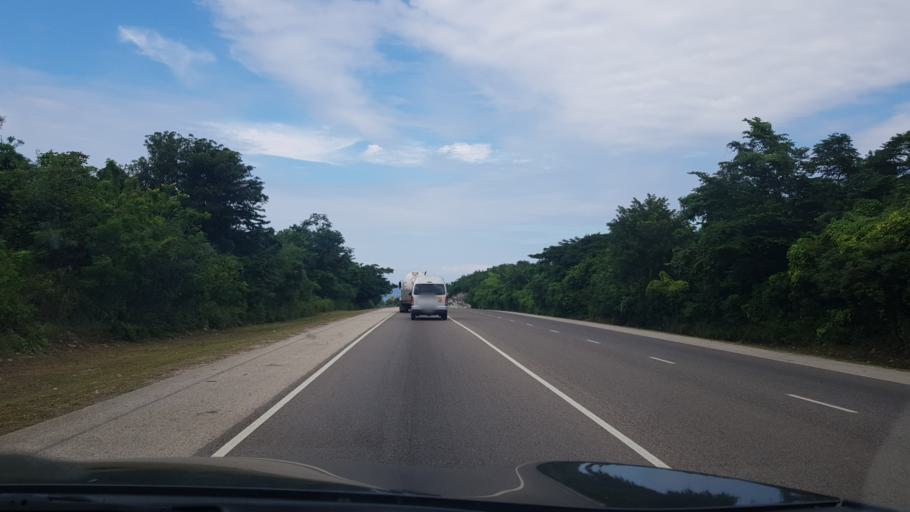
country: JM
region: Trelawny
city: Duncans
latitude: 18.4806
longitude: -77.5956
